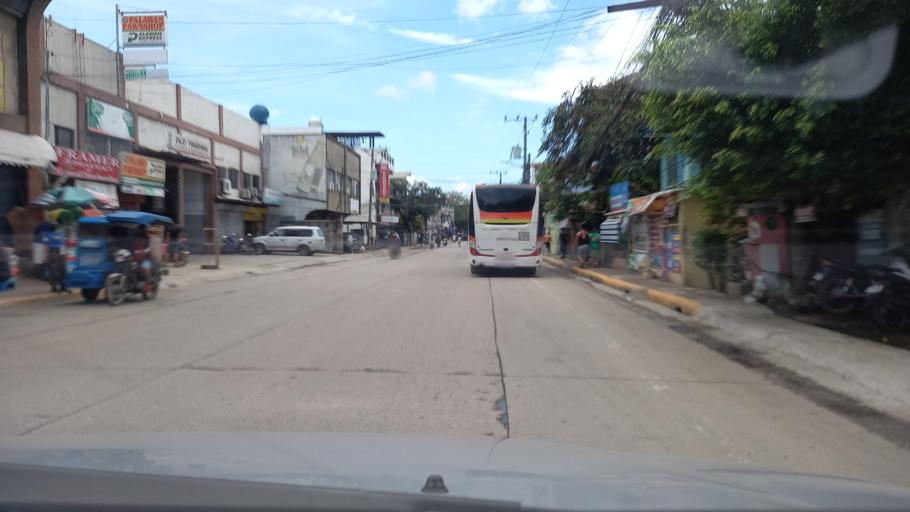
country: PH
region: Central Visayas
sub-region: Lapu-Lapu City
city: Buagsong
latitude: 10.3266
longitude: 123.9422
